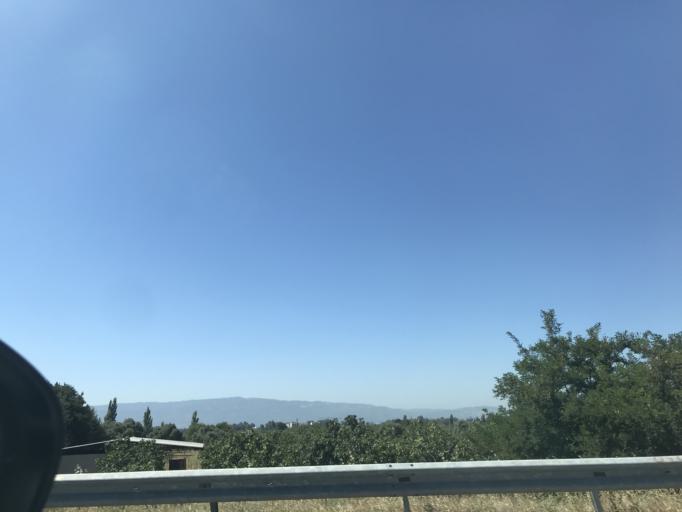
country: TR
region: Aydin
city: Incirliova
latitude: 37.8700
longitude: 27.7135
